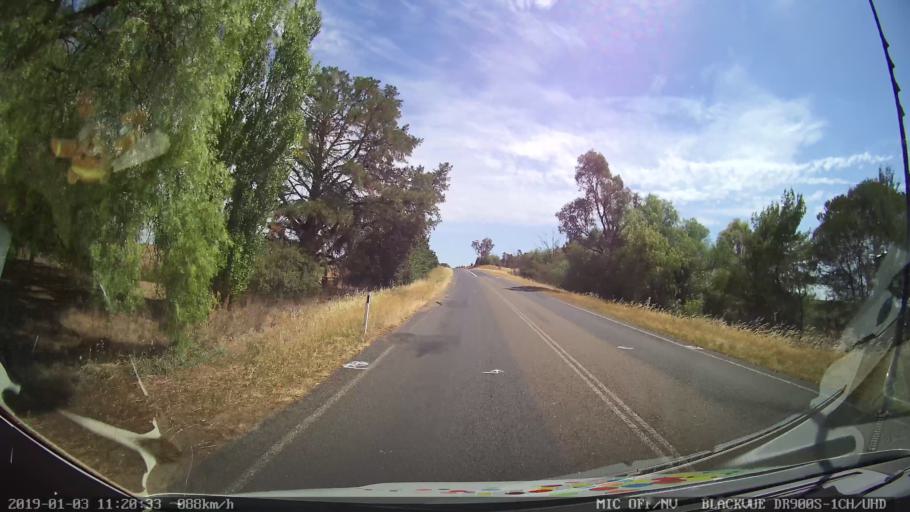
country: AU
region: New South Wales
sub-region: Young
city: Young
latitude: -34.0996
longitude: 148.2545
